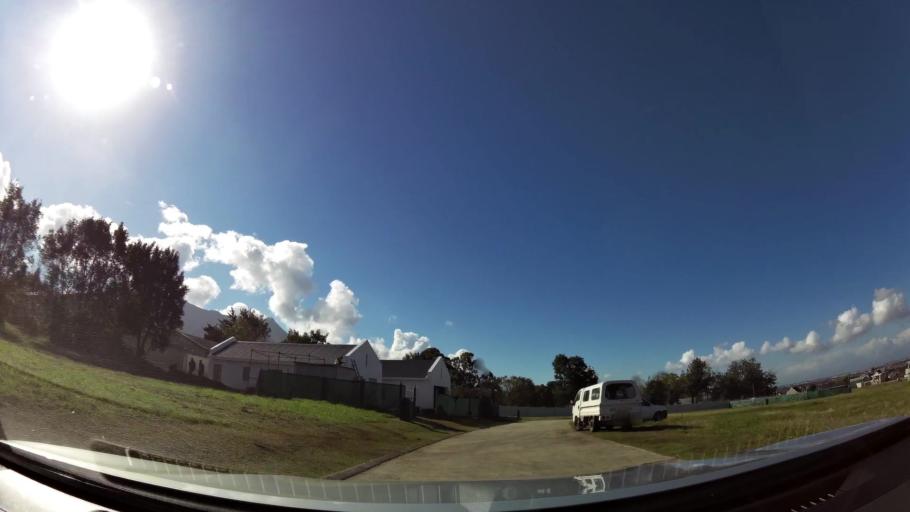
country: ZA
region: Western Cape
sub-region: Eden District Municipality
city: George
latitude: -33.9405
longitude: 22.4045
